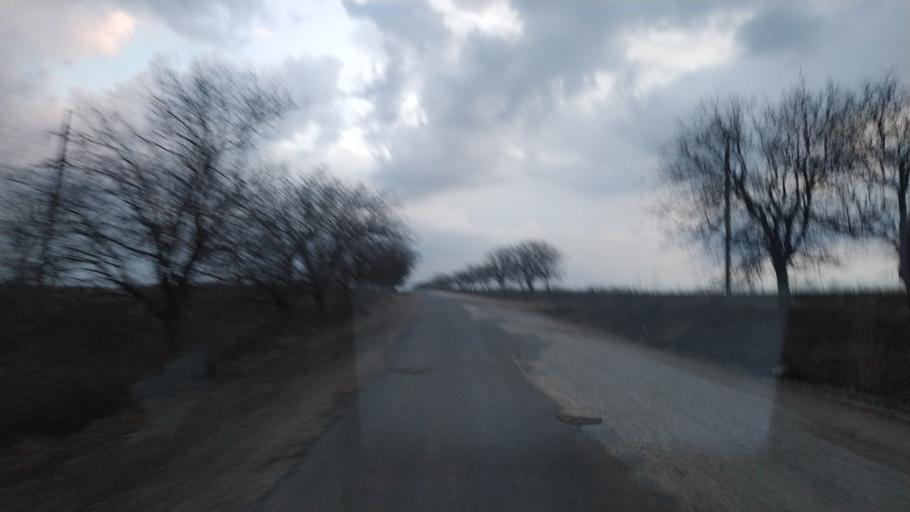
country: MD
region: Anenii Noi
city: Anenii Noi
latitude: 46.9679
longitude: 29.2847
